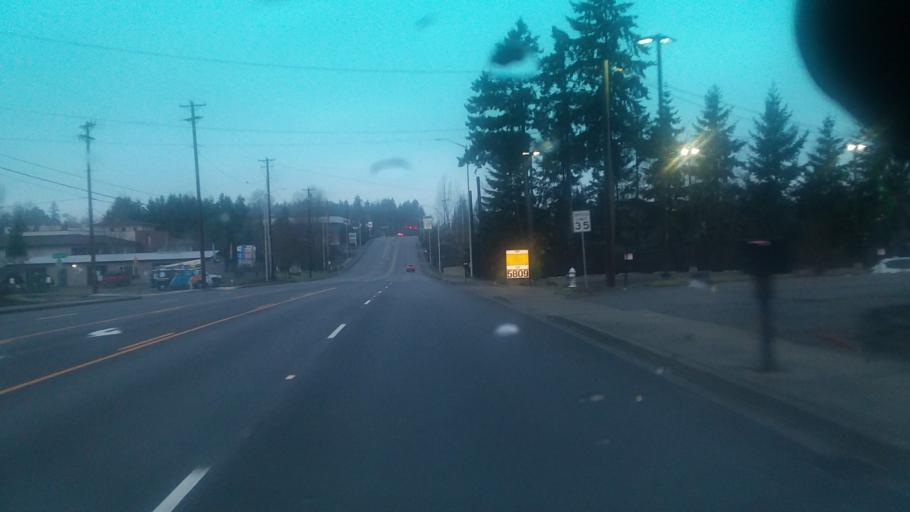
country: US
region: Washington
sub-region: Pierce County
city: Summit
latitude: 47.1547
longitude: -122.3510
